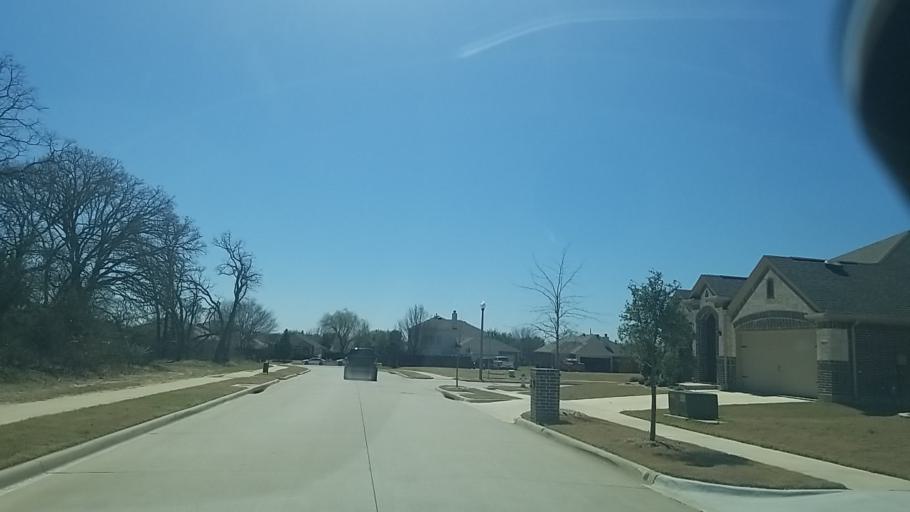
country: US
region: Texas
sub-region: Denton County
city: Corinth
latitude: 33.1564
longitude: -97.1105
